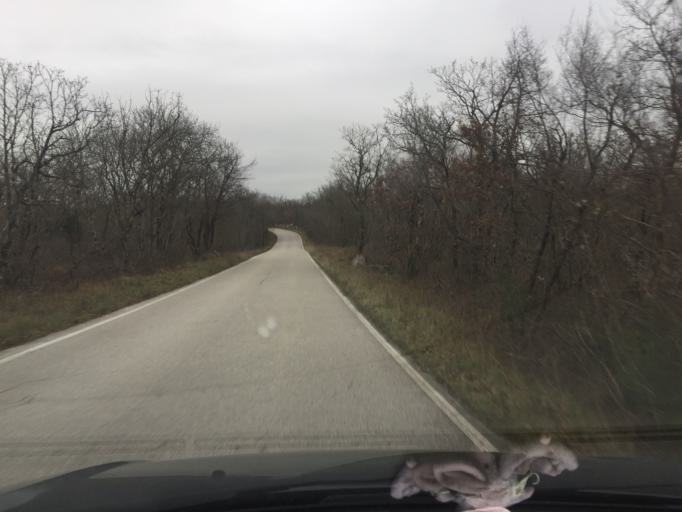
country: IT
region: Friuli Venezia Giulia
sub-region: Provincia di Trieste
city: Zolla
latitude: 45.7102
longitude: 13.8130
